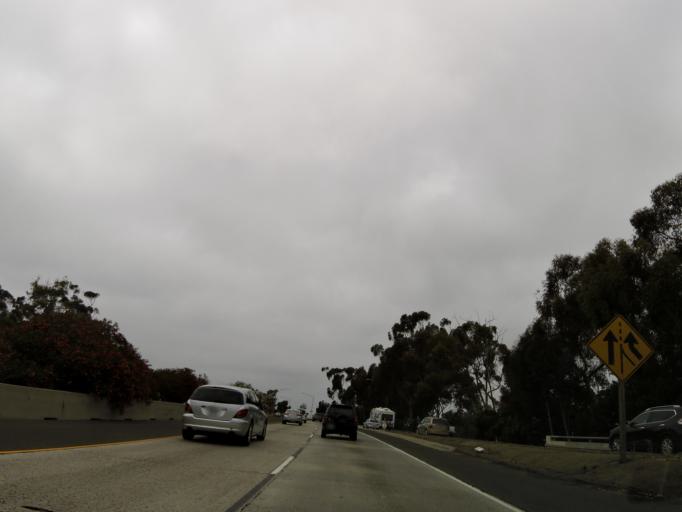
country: US
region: California
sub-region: Ventura County
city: Ventura
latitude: 34.2650
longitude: -119.2412
